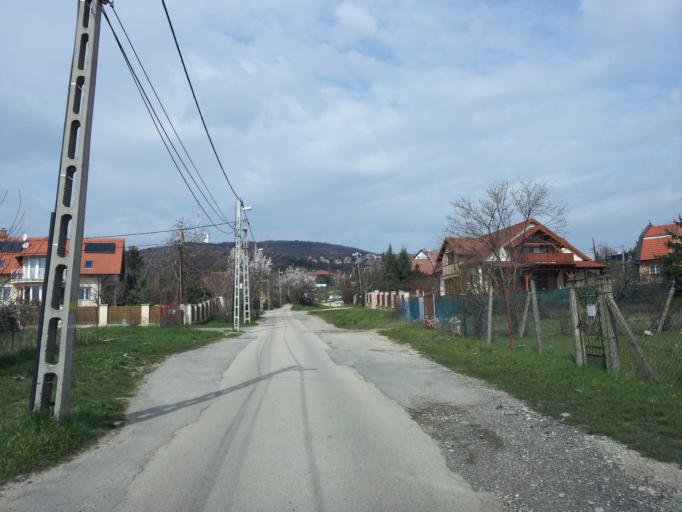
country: HU
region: Pest
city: Budaors
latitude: 47.4740
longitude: 18.9862
